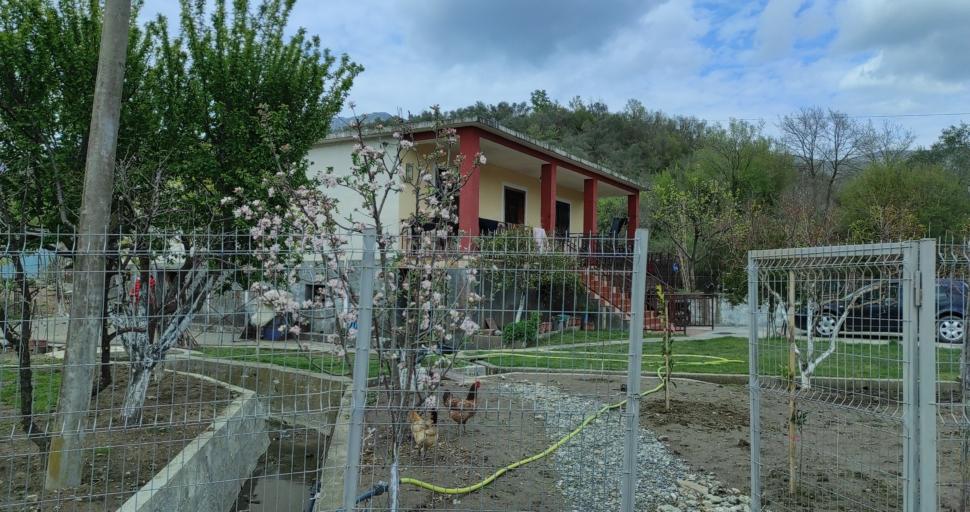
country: AL
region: Shkoder
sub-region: Rrethi i Shkodres
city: Dajc
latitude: 42.0336
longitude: 19.4116
